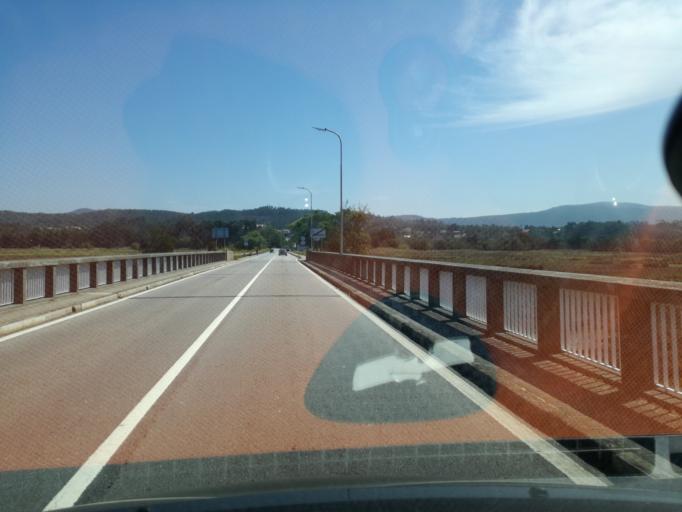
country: ES
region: Galicia
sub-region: Provincia de Pontevedra
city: A Guarda
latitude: 41.8789
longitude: -8.8317
